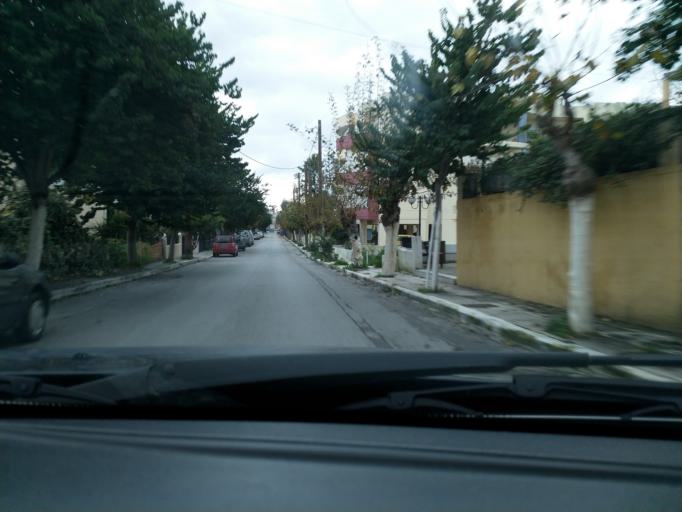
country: GR
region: Crete
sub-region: Nomos Chanias
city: Chania
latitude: 35.5111
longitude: 24.0359
